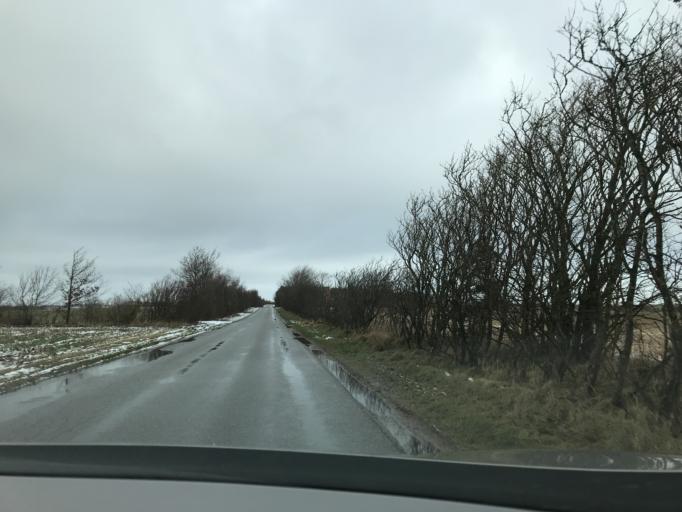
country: DK
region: South Denmark
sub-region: Varde Kommune
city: Varde
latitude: 55.6519
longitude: 8.4125
